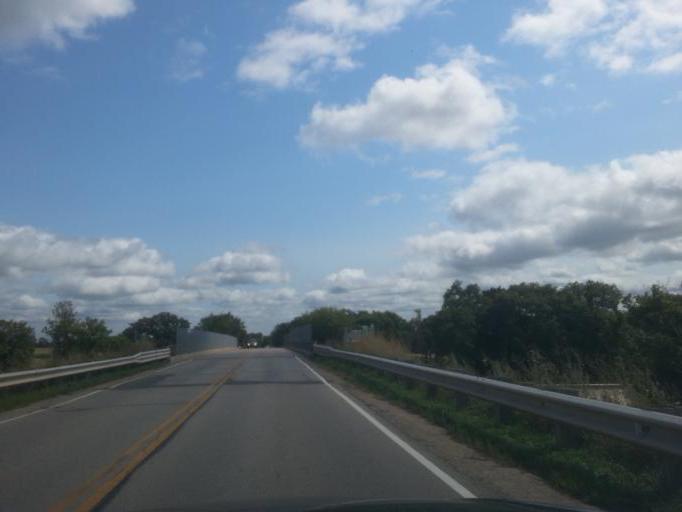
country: US
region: Wisconsin
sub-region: Dane County
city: Monona
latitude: 43.0990
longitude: -89.2851
